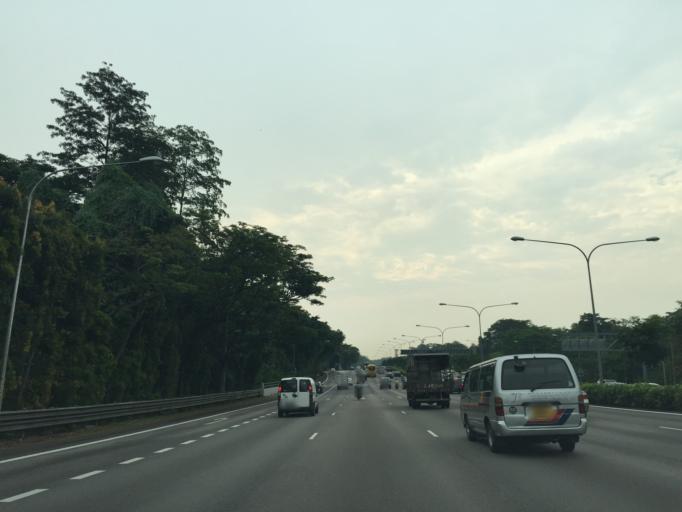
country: SG
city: Singapore
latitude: 1.3364
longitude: 103.8093
